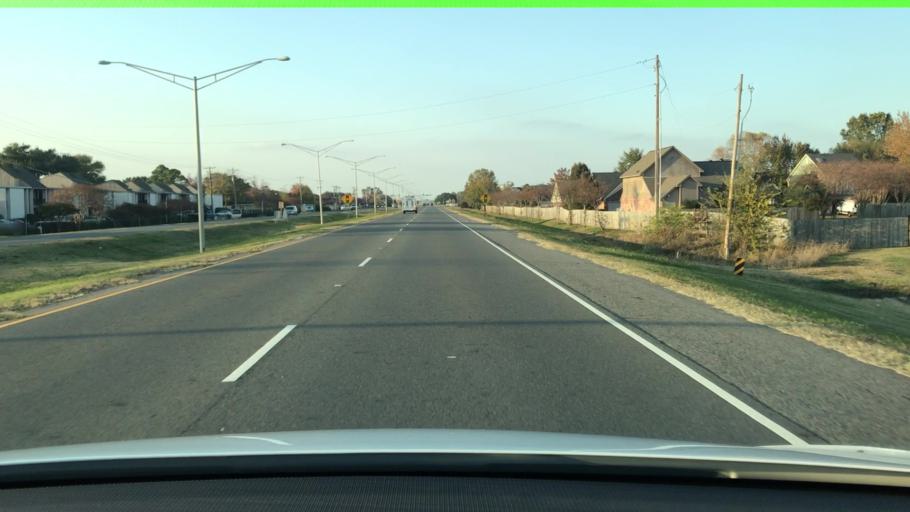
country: US
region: Louisiana
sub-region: Bossier Parish
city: Bossier City
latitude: 32.4095
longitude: -93.6988
